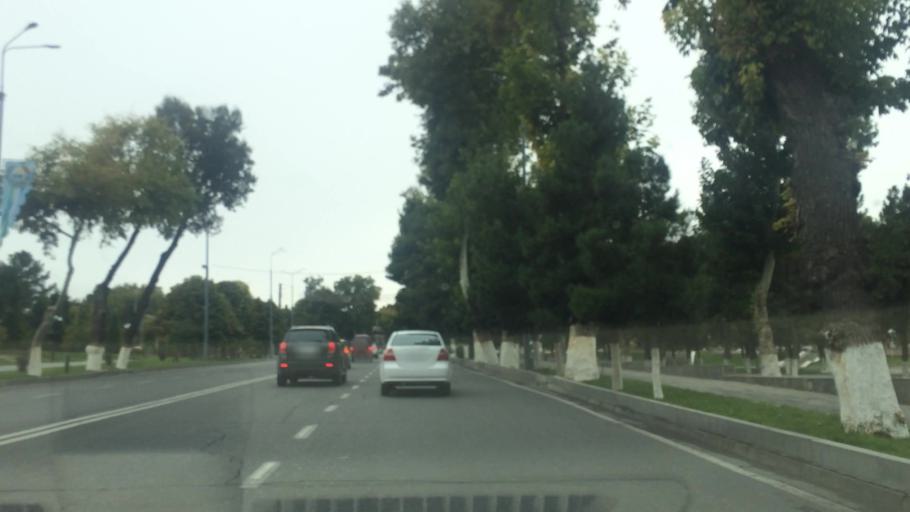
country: UZ
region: Samarqand
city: Samarqand
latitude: 39.6513
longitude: 66.9673
